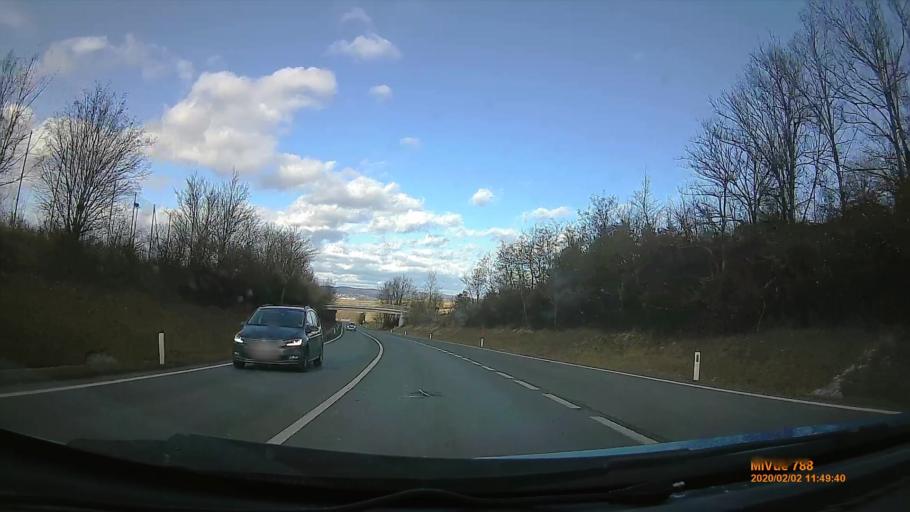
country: AT
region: Burgenland
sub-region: Eisenstadt-Umgebung
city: Klingenbach
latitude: 47.7549
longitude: 16.5473
